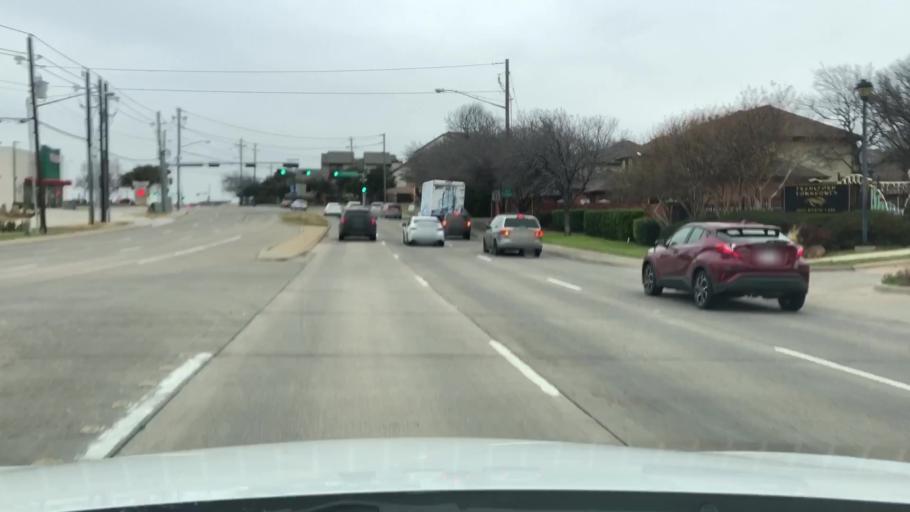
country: US
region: Texas
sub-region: Dallas County
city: Addison
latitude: 32.9982
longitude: -96.8558
